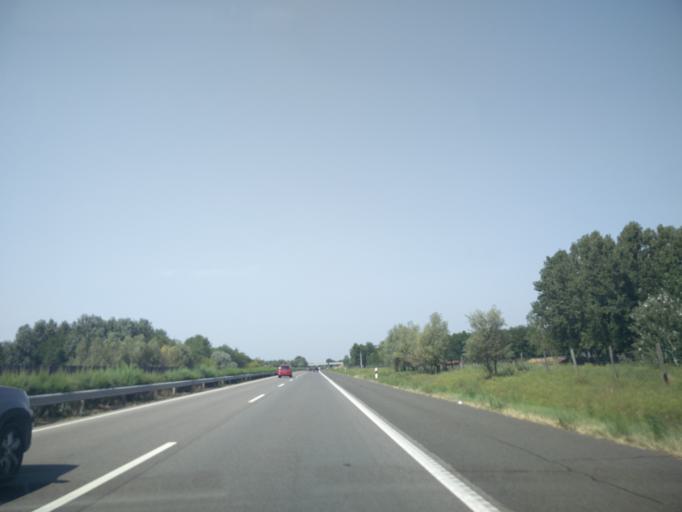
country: HU
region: Csongrad
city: Szatymaz
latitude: 46.3338
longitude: 20.0236
